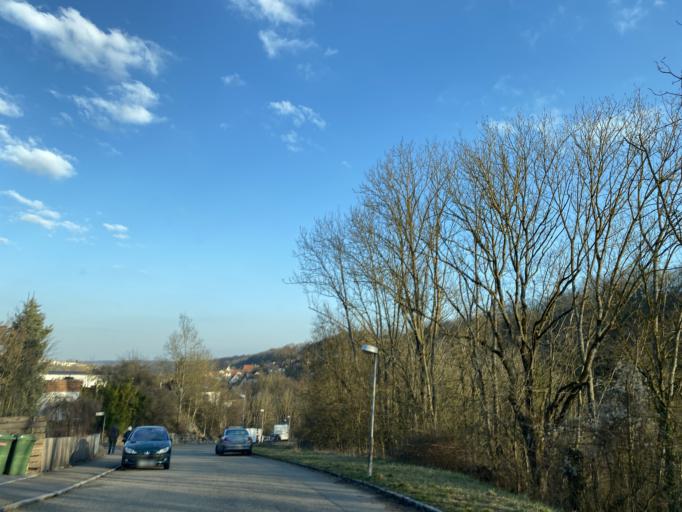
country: DE
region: Baden-Wuerttemberg
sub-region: Regierungsbezirk Stuttgart
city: Vaihingen an der Enz
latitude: 48.9149
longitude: 8.9371
